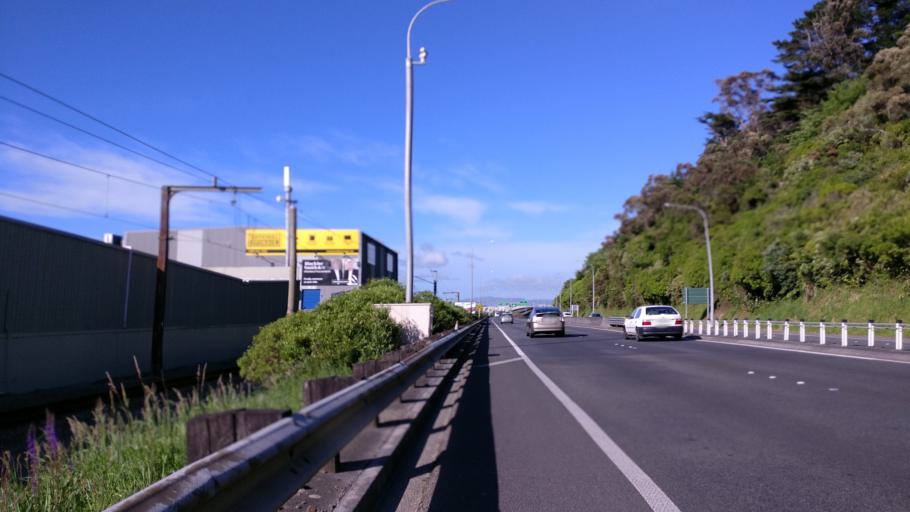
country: NZ
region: Wellington
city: Petone
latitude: -41.2126
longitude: 174.8887
